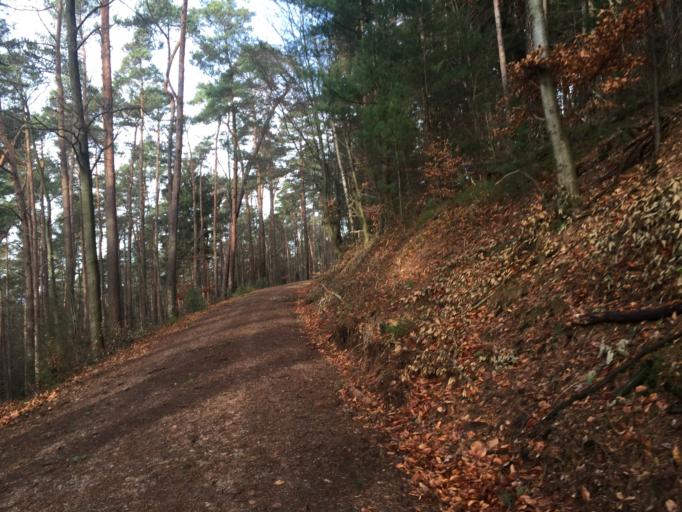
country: DE
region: Hesse
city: Reichelsheim
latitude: 49.6969
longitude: 8.8925
